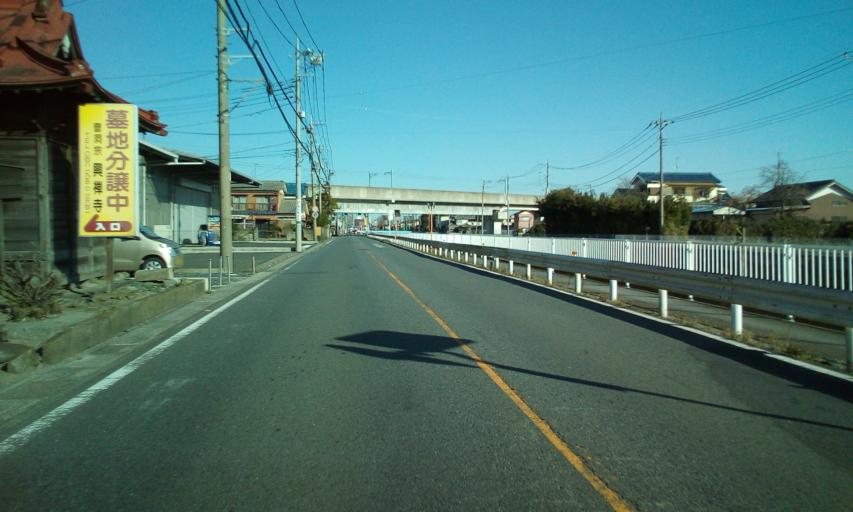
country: JP
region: Chiba
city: Nagareyama
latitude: 35.8286
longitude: 139.8830
